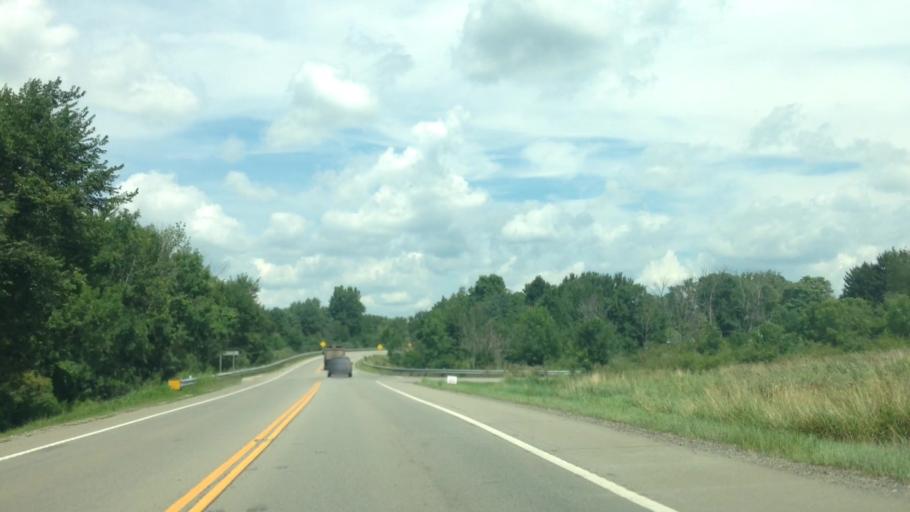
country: US
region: Ohio
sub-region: Wayne County
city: Doylestown
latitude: 40.9509
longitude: -81.7398
